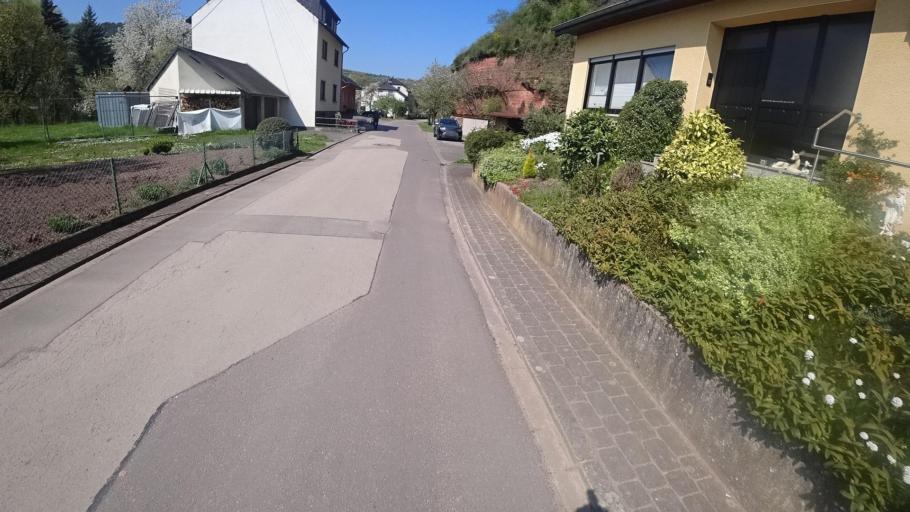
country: DE
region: Rheinland-Pfalz
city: Tawern
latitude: 49.6749
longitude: 6.5154
